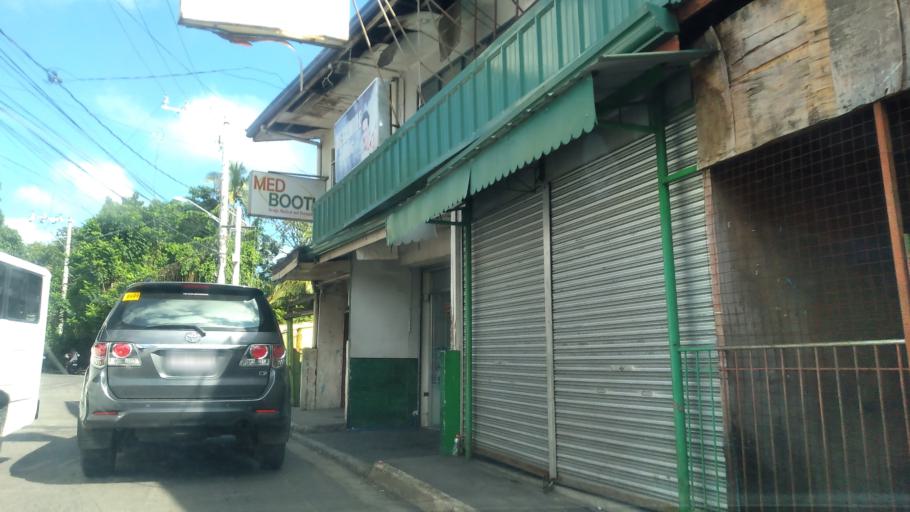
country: PH
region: Calabarzon
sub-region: Province of Quezon
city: Lucena
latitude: 13.9407
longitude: 121.6120
